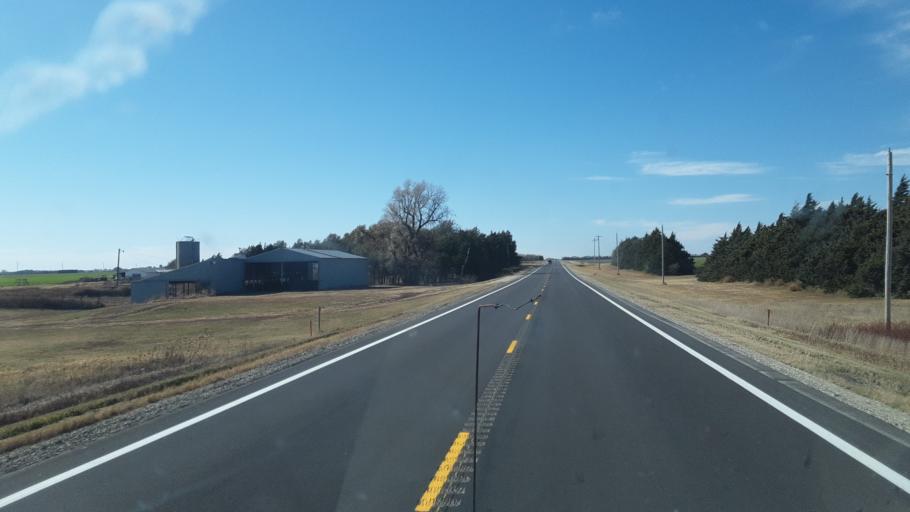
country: US
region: Kansas
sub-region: Rice County
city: Lyons
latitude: 38.3766
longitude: -98.0961
